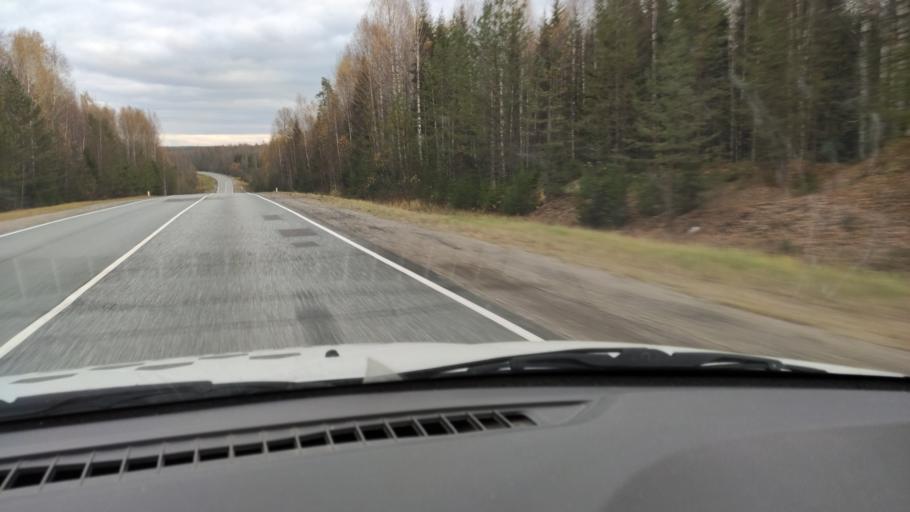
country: RU
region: Kirov
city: Dubrovka
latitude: 58.8941
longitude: 51.3325
